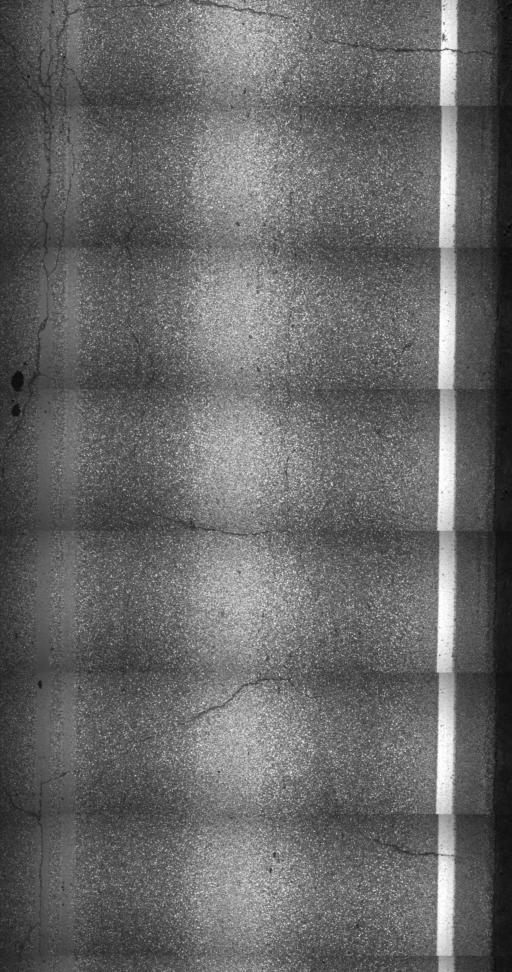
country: US
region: Vermont
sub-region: Windsor County
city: Chester
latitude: 43.2680
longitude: -72.6173
